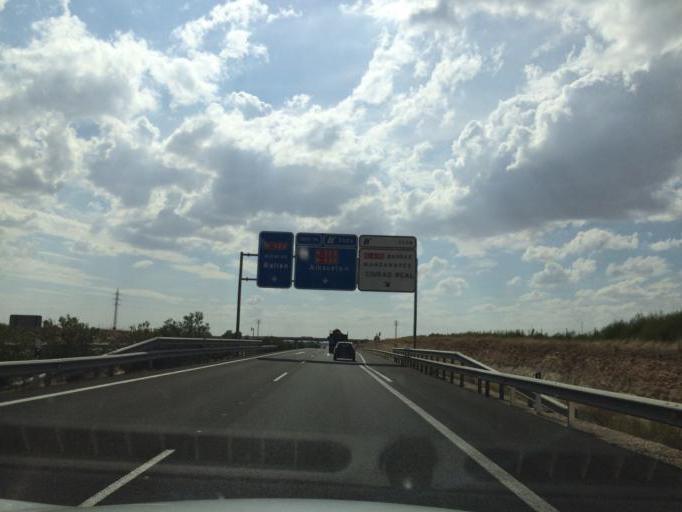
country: ES
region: Castille-La Mancha
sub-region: Provincia de Albacete
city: Albacete
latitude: 39.0040
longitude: -1.8975
